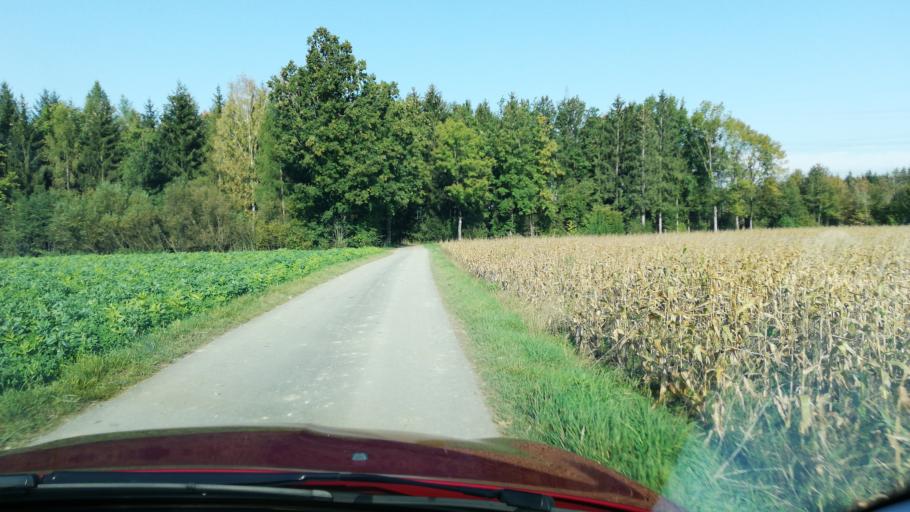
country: AT
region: Upper Austria
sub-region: Politischer Bezirk Kirchdorf an der Krems
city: Kremsmunster
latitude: 48.0993
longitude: 14.1580
